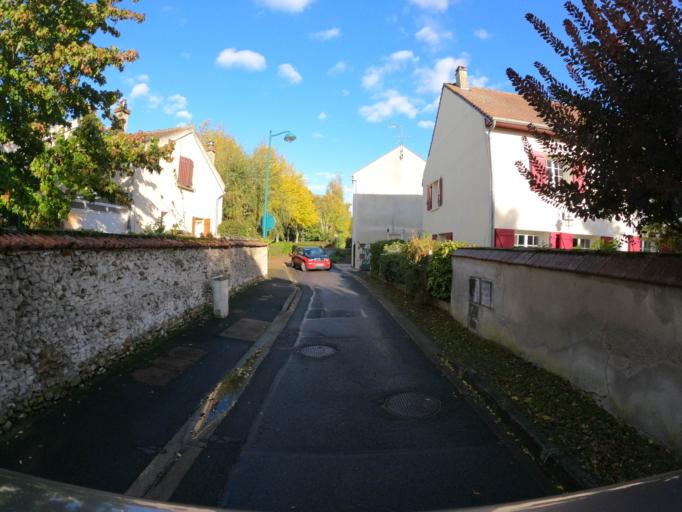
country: FR
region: Ile-de-France
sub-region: Departement de Seine-et-Marne
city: Bailly-Romainvilliers
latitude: 48.8466
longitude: 2.8248
